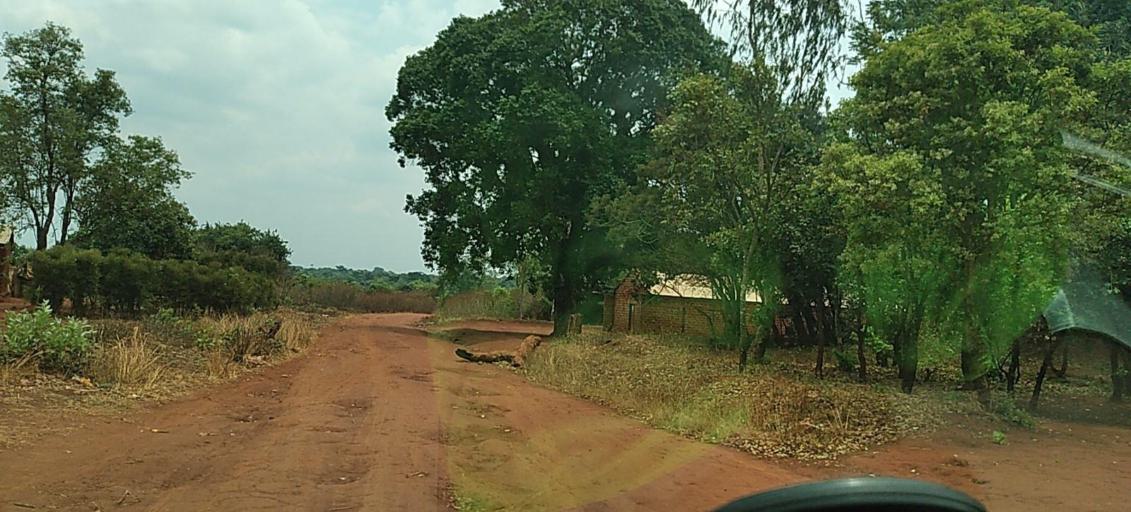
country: ZM
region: North-Western
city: Kansanshi
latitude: -12.0442
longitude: 26.3915
